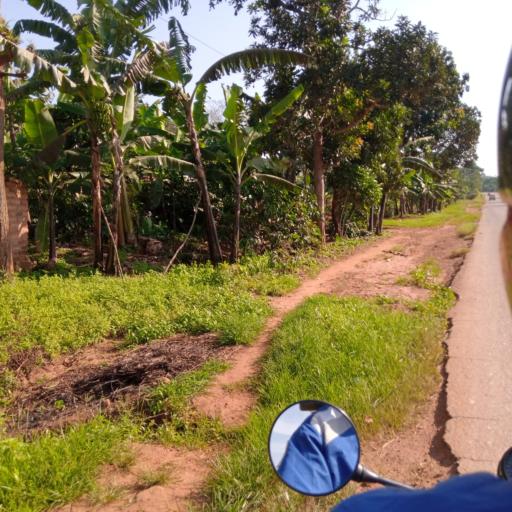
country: UG
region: Central Region
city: Masaka
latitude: -0.4539
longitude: 31.6672
